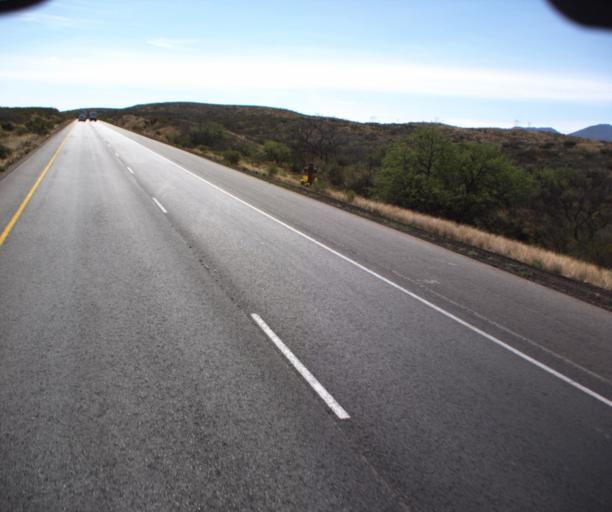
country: US
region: Arizona
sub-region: Cochise County
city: Mescal
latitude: 31.9702
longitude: -110.4836
